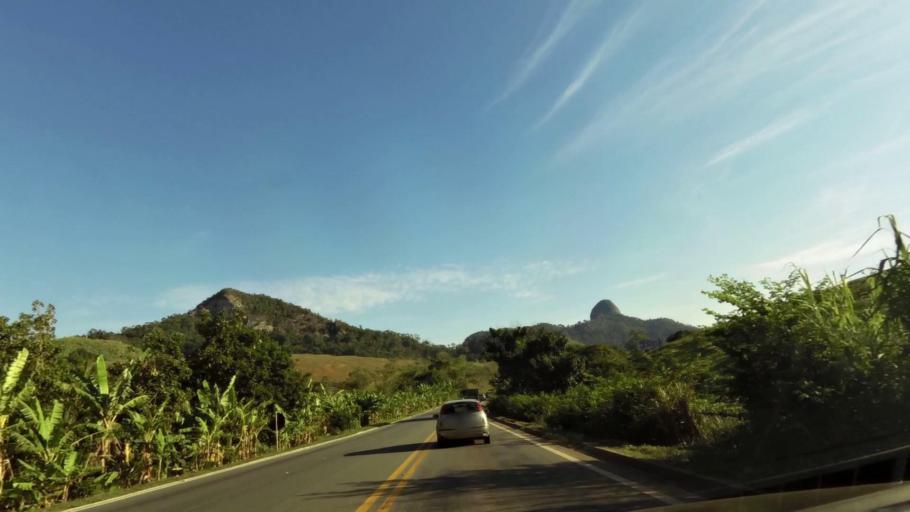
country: BR
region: Espirito Santo
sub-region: Guarapari
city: Guarapari
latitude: -20.5354
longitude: -40.4833
